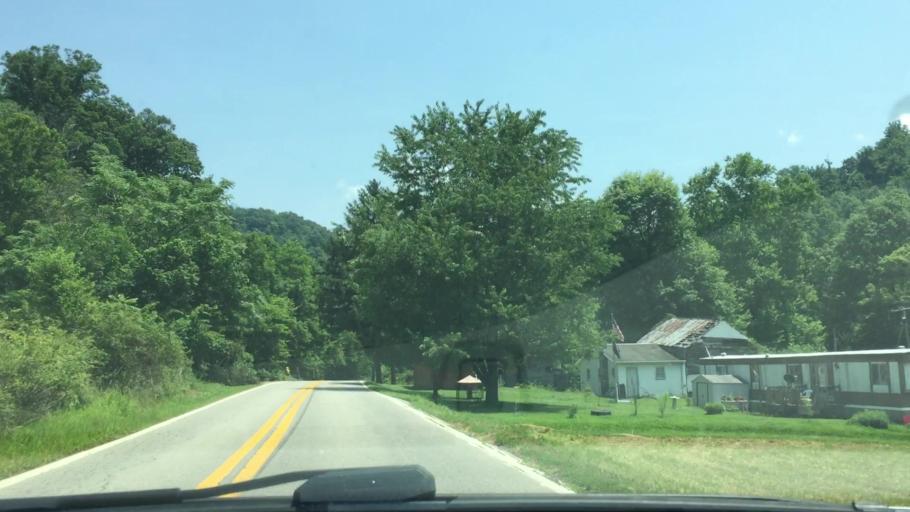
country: US
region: West Virginia
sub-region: Wetzel County
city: New Martinsville
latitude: 39.6895
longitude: -80.7967
